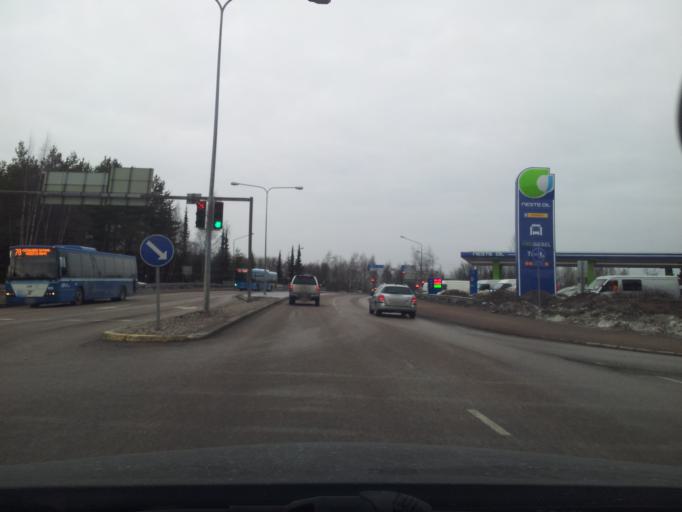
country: FI
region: Uusimaa
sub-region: Helsinki
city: Vantaa
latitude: 60.2406
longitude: 25.0207
